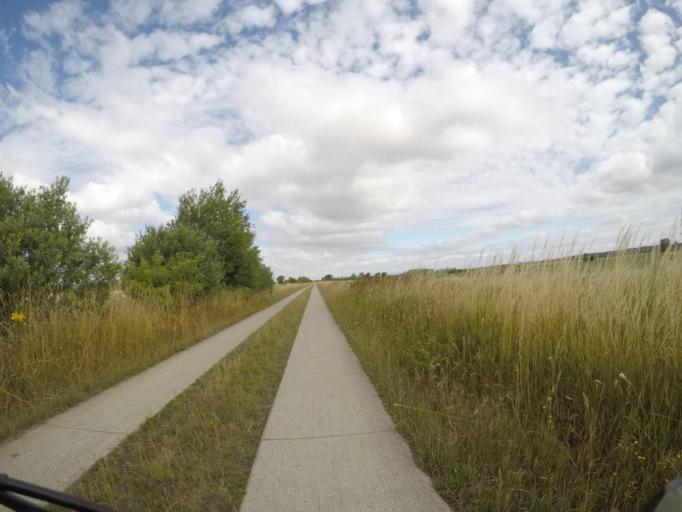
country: DE
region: Lower Saxony
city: Hitzacker
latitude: 53.1739
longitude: 11.0496
